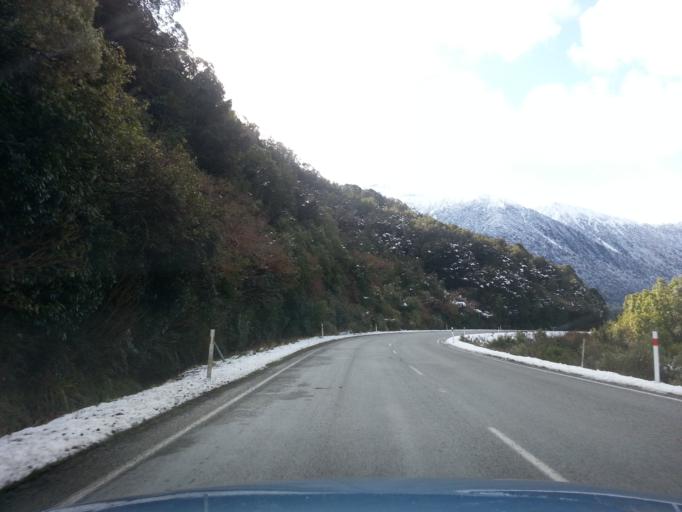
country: NZ
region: West Coast
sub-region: Grey District
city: Greymouth
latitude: -42.8195
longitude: 171.5634
